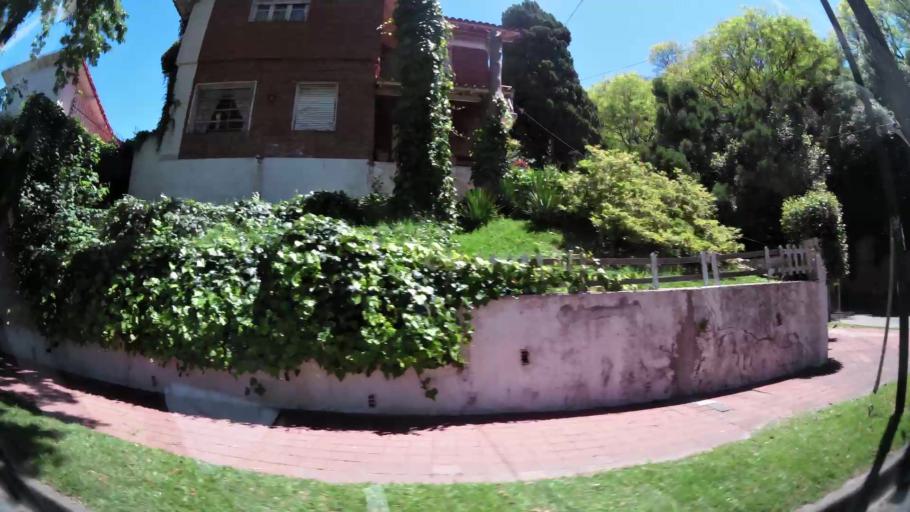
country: AR
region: Buenos Aires
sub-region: Partido de San Isidro
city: San Isidro
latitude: -34.4521
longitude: -58.5236
